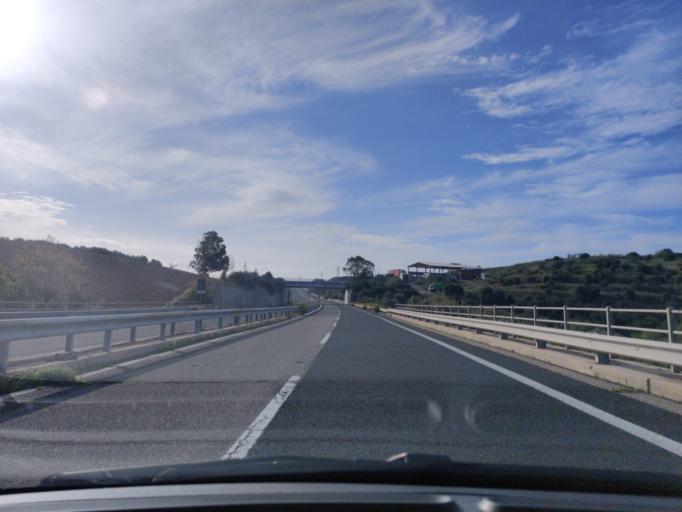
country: IT
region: Latium
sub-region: Citta metropolitana di Roma Capitale
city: Aurelia
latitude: 42.1216
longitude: 11.7913
